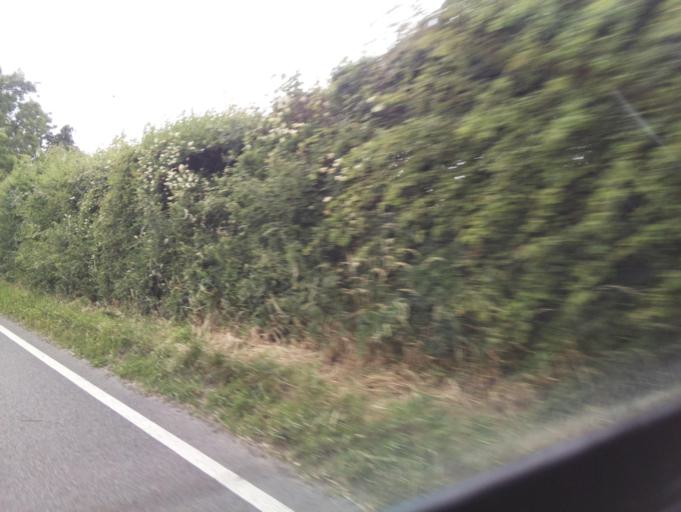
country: GB
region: England
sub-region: Somerset
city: Stoke-sub-Hamdon
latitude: 50.9097
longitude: -2.7379
